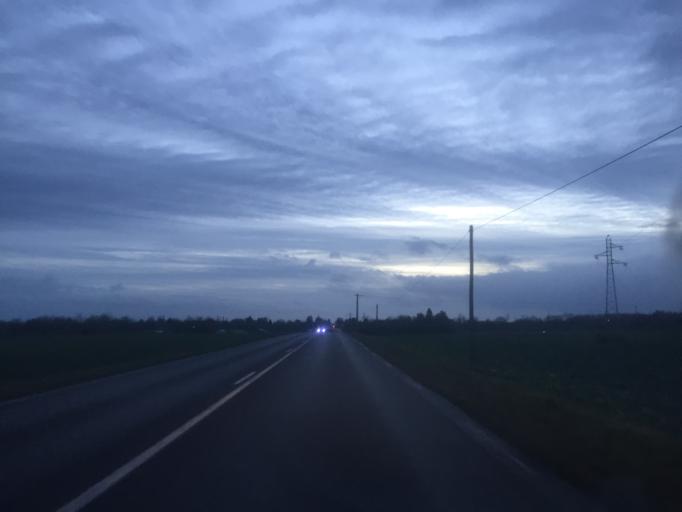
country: FR
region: Franche-Comte
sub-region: Departement du Jura
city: Dole
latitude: 47.1084
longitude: 5.5233
